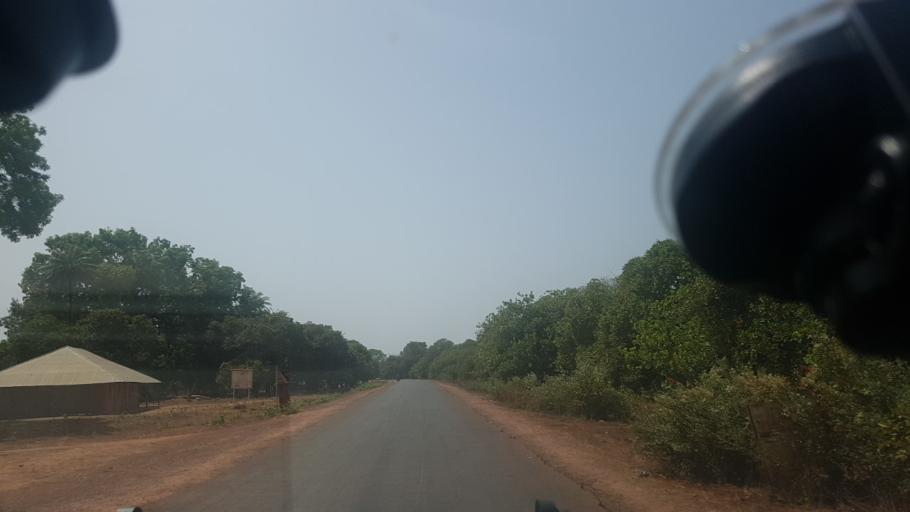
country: GW
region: Cacheu
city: Cacheu
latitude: 12.4125
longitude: -16.0718
